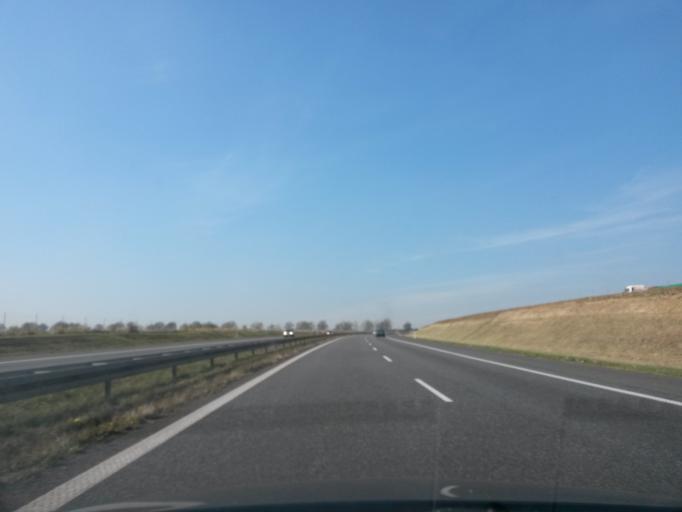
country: PL
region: Silesian Voivodeship
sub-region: Powiat gliwicki
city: Zernica
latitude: 50.2683
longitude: 18.5851
